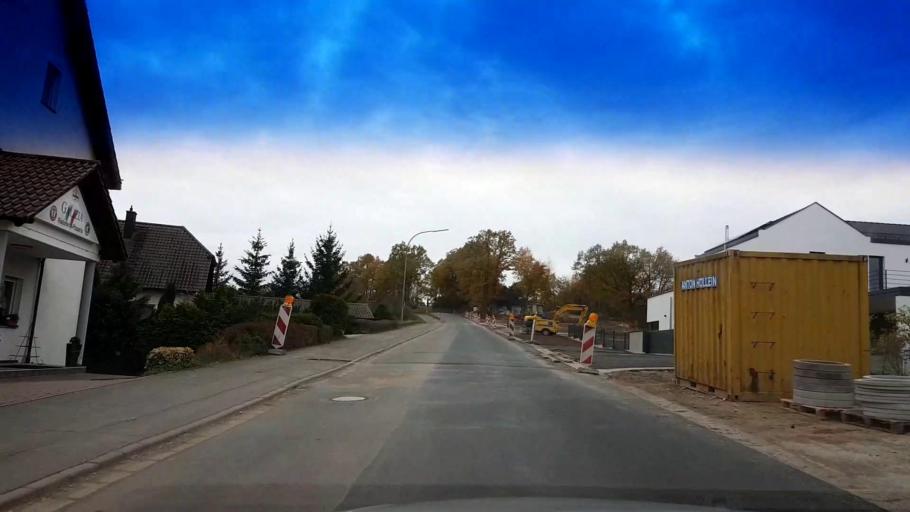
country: DE
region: Bavaria
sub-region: Upper Franconia
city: Viereth-Trunstadt
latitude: 49.9183
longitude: 10.7697
